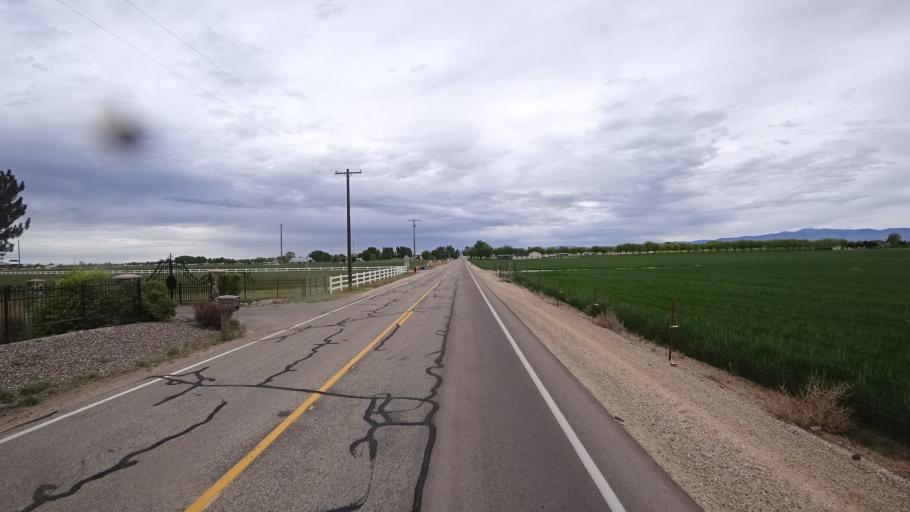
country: US
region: Idaho
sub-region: Ada County
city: Meridian
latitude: 43.5677
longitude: -116.4137
